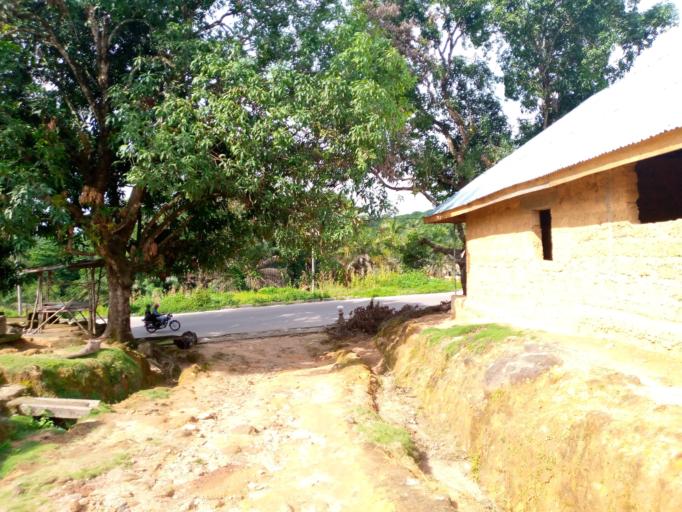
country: SL
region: Northern Province
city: Magburaka
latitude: 8.7288
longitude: -11.9468
